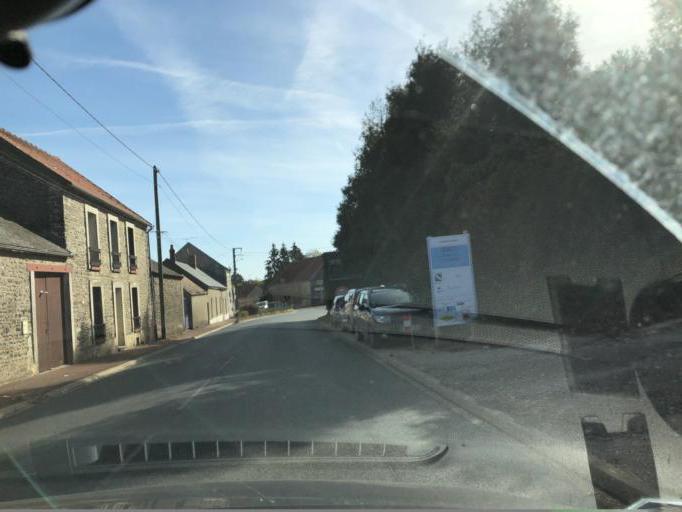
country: FR
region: Centre
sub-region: Departement du Loiret
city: Sermaises
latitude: 48.3582
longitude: 2.2705
